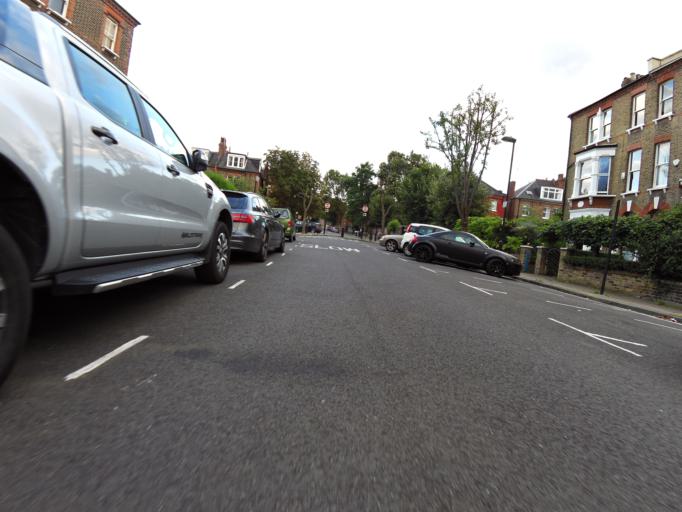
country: GB
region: England
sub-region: Greater London
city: Holloway
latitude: 51.5560
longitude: -0.1300
